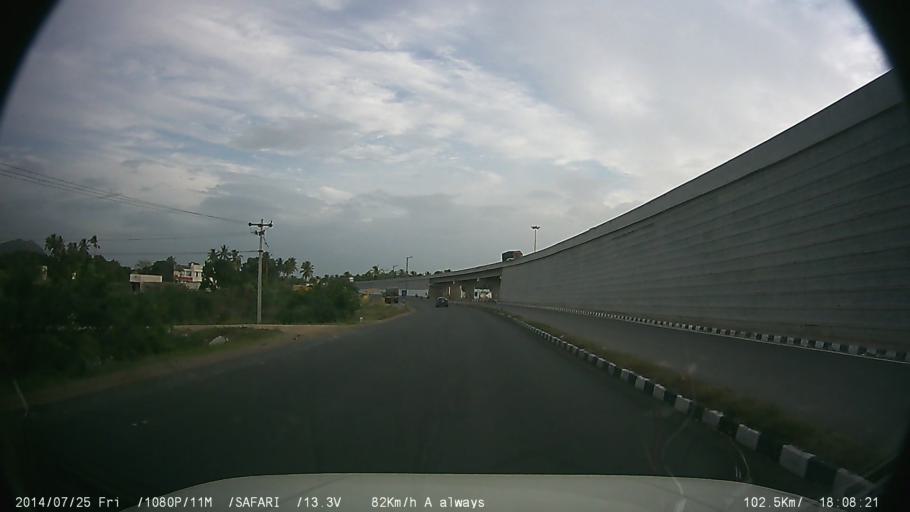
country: IN
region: Tamil Nadu
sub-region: Krishnagiri
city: Kaverippattanam
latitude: 12.4021
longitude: 78.2192
